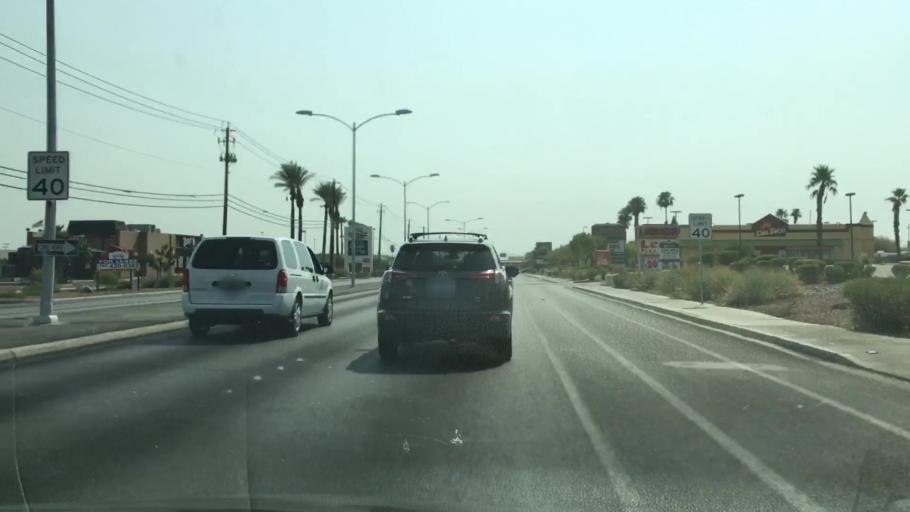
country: US
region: Nevada
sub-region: Clark County
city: Whitney
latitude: 36.0709
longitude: -115.0771
